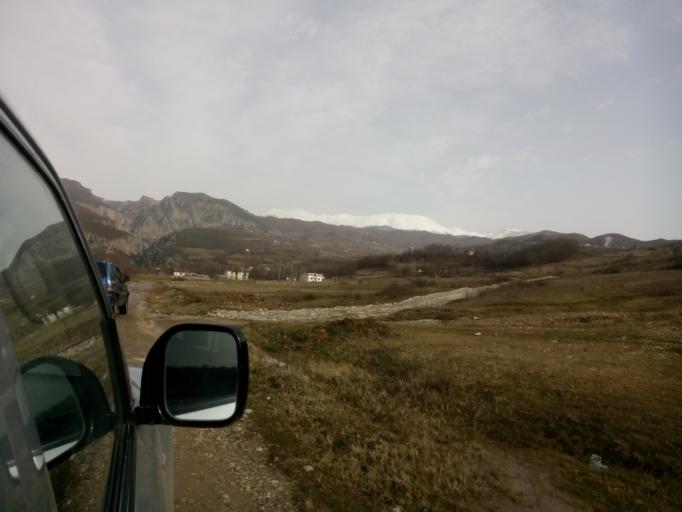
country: AL
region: Diber
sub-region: Rrethi i Matit
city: Rukaj
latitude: 41.6873
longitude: 19.9984
